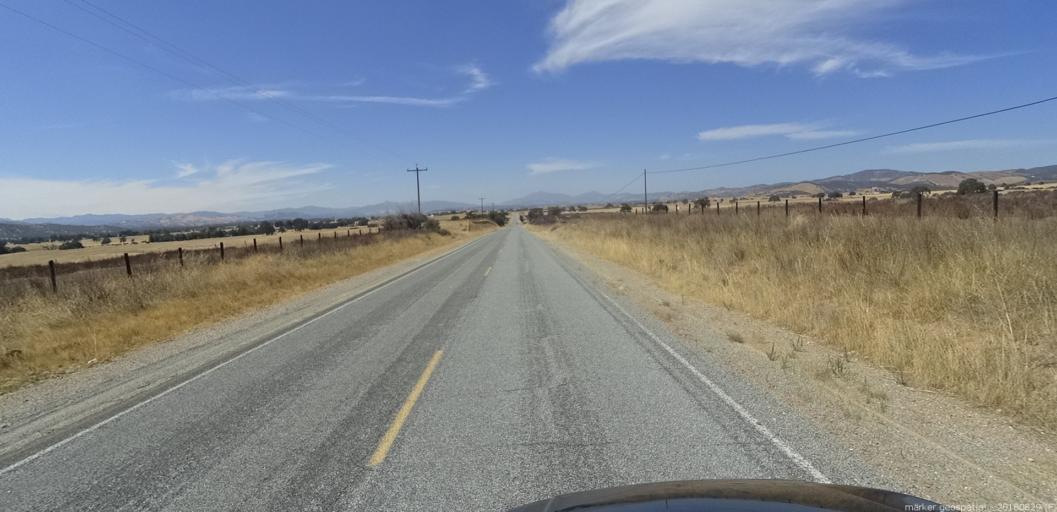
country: US
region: California
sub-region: San Luis Obispo County
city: Lake Nacimiento
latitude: 35.9268
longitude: -121.0455
